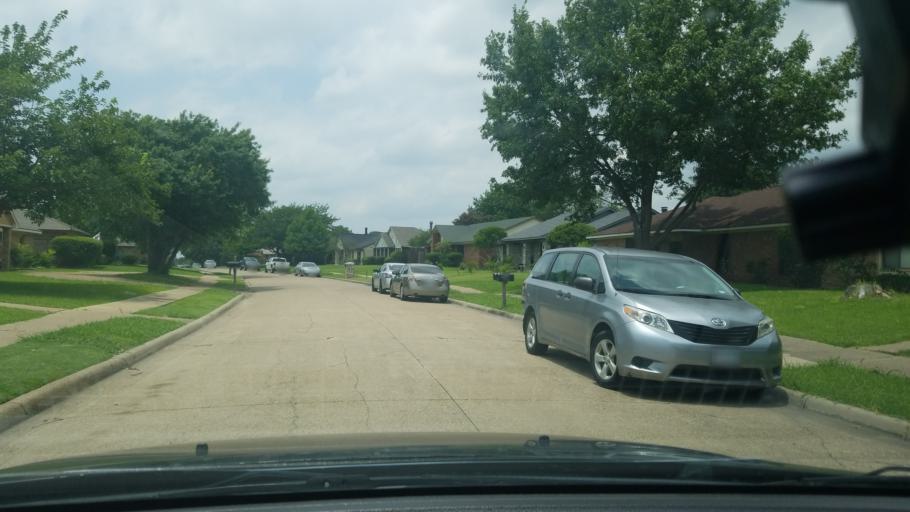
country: US
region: Texas
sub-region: Dallas County
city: Mesquite
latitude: 32.8000
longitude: -96.6193
